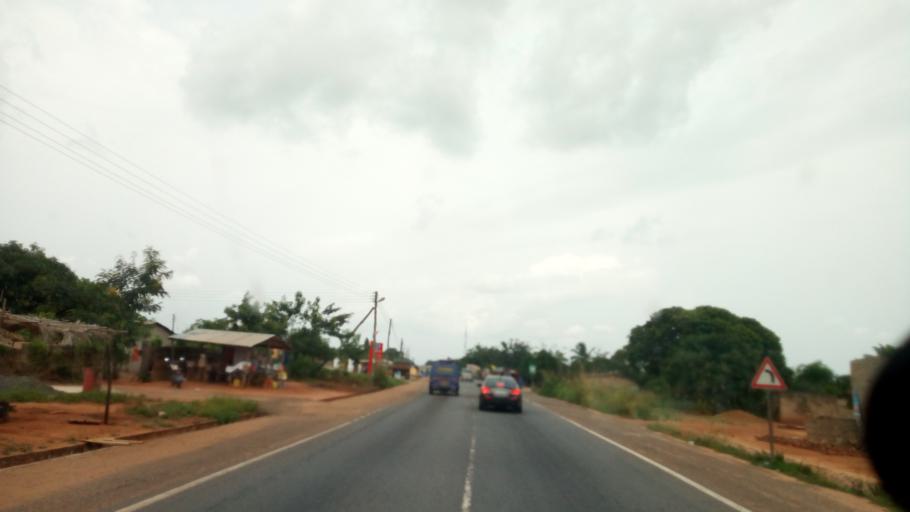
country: GH
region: Volta
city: Keta
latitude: 6.0641
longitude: 0.9079
